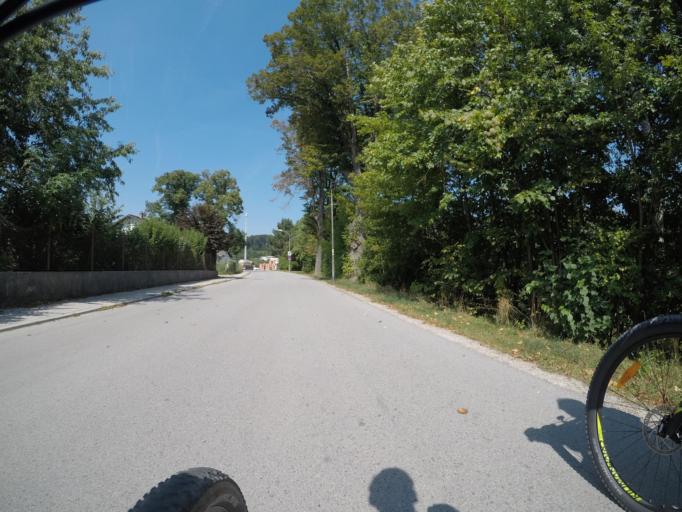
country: AT
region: Lower Austria
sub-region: Politischer Bezirk Baden
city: Pottenstein
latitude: 47.9610
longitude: 16.0906
